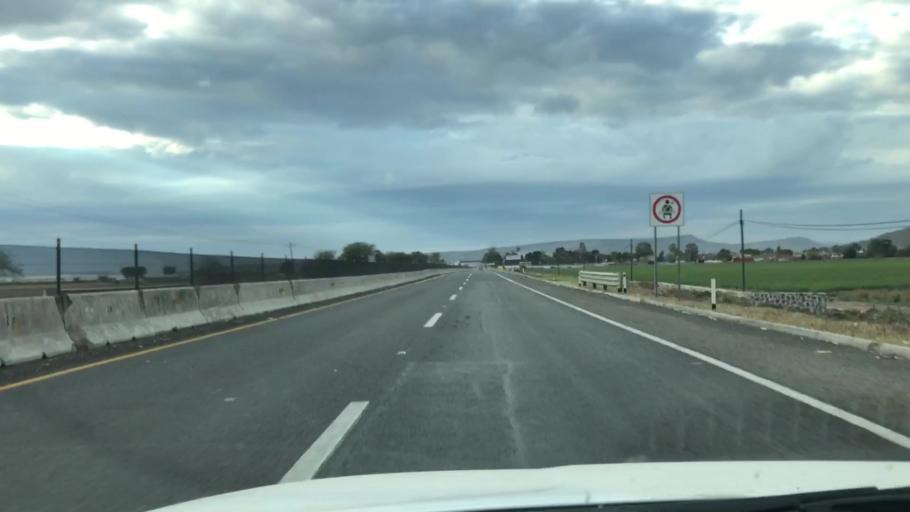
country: MX
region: Guanajuato
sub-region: Penjamo
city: Estacion la Piedad
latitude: 20.3865
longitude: -101.9132
